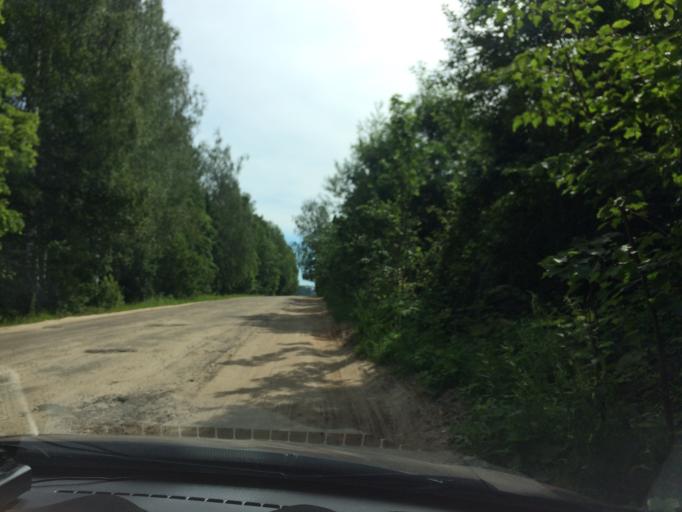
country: RU
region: Mariy-El
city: Mochalishche
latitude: 56.5458
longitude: 48.3812
